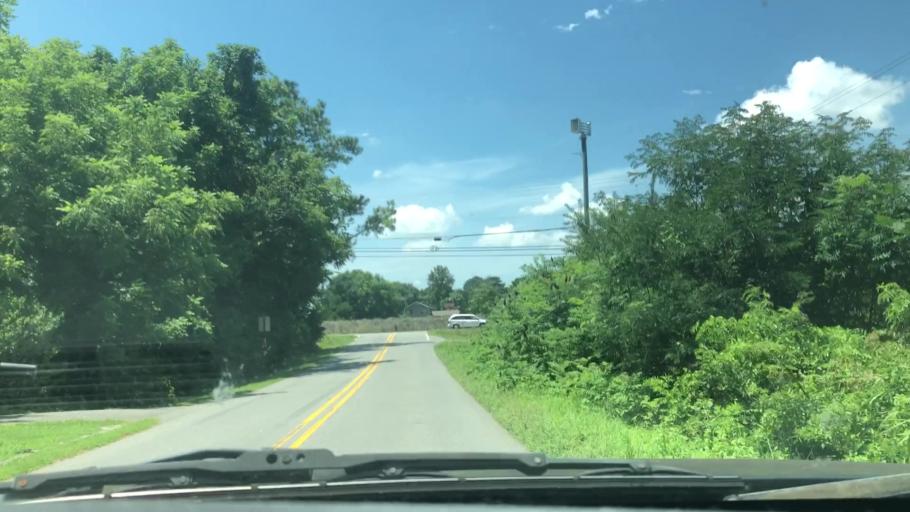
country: US
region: Georgia
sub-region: Bartow County
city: Rydal
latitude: 34.3215
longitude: -84.7185
